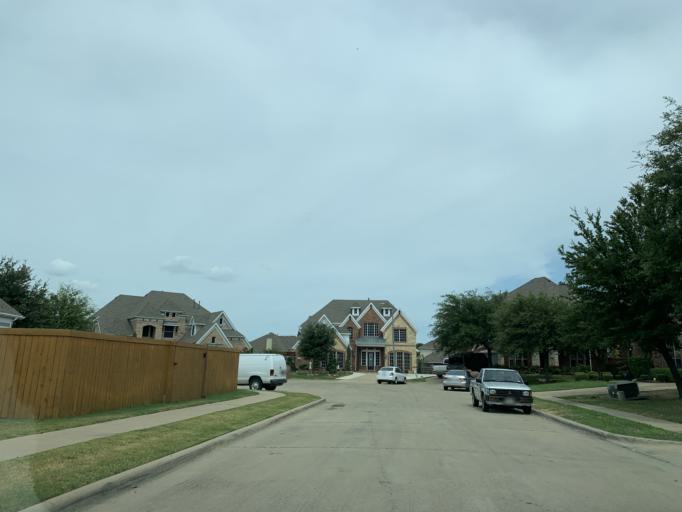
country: US
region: Texas
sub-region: Dallas County
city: Grand Prairie
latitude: 32.6558
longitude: -97.0370
